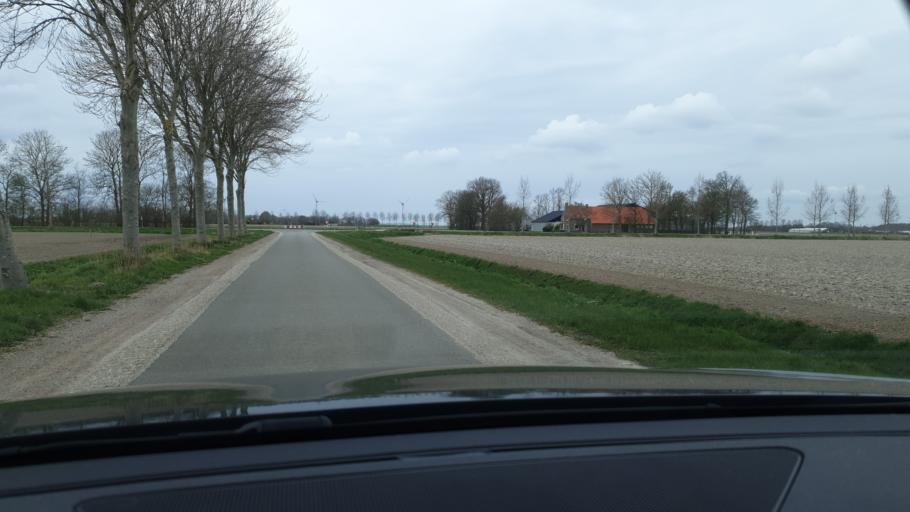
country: NL
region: Flevoland
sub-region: Gemeente Urk
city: Urk
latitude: 52.7095
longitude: 5.6598
